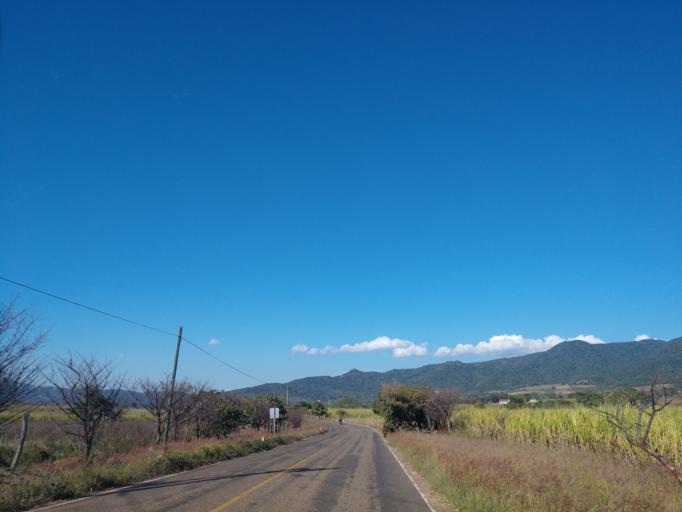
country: MX
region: Nayarit
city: Compostela
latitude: 21.2649
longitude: -104.8930
